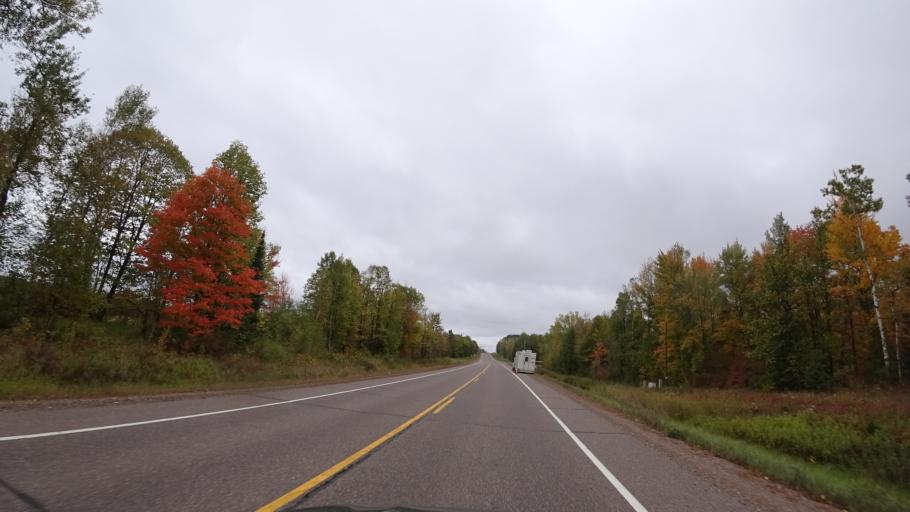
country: US
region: Wisconsin
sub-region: Rusk County
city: Ladysmith
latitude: 45.5725
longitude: -91.1116
